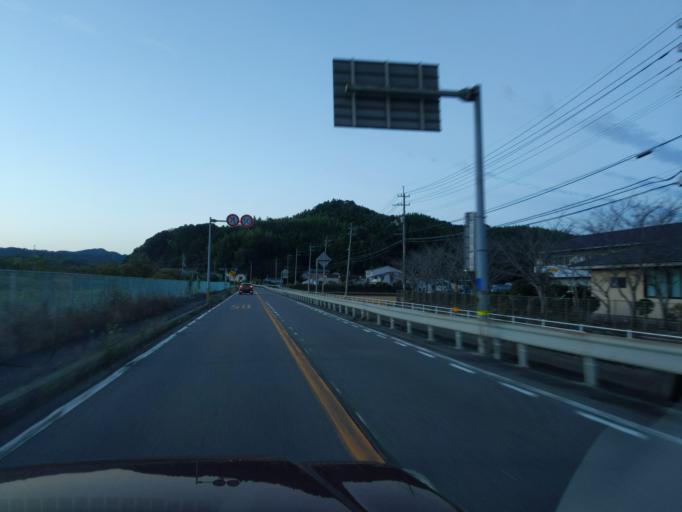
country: JP
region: Tokushima
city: Anan
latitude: 33.8597
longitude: 134.6271
